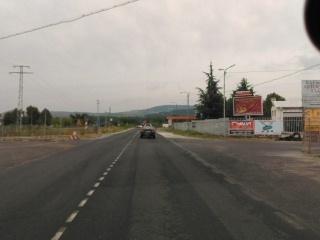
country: BG
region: Plovdiv
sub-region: Obshtina Karlovo
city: Karlovo
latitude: 42.5472
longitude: 24.8264
